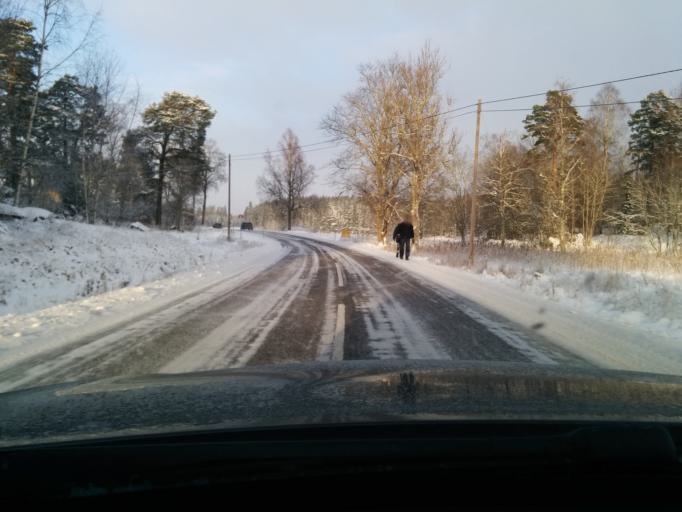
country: SE
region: Uppsala
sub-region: Tierps Kommun
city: Orbyhus
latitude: 60.2026
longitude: 17.7011
